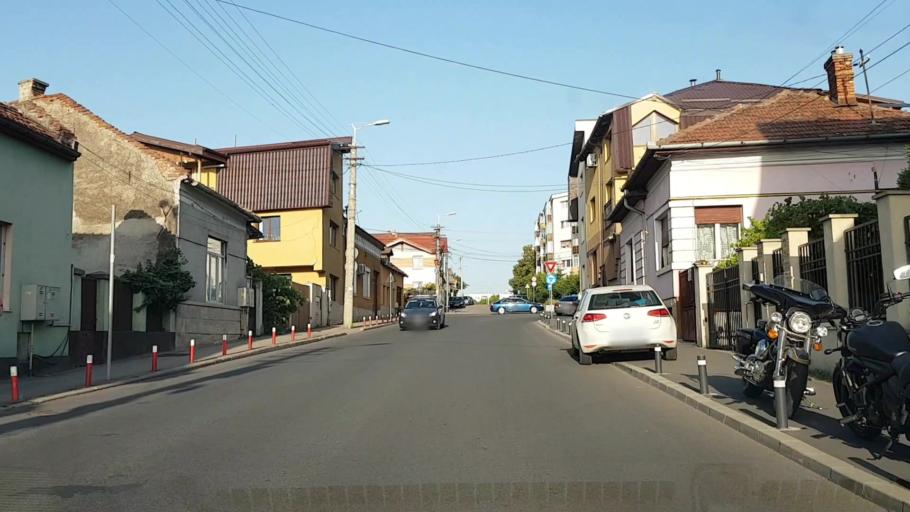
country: RO
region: Cluj
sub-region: Municipiul Cluj-Napoca
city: Cluj-Napoca
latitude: 46.7718
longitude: 23.6080
